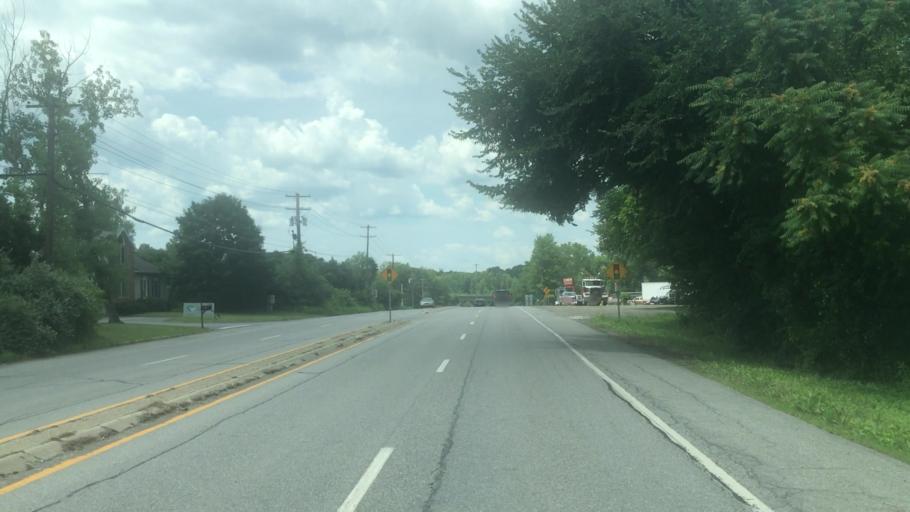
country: US
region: New York
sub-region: Putnam County
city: Brewster
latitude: 41.3914
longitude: -73.5928
